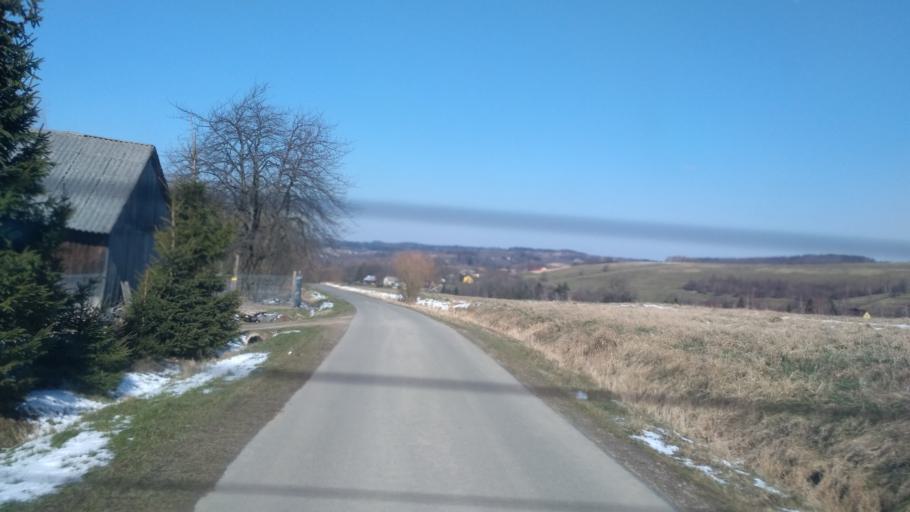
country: PL
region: Subcarpathian Voivodeship
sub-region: Powiat strzyzowski
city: Gwoznica Gorna
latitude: 49.8219
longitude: 22.0100
